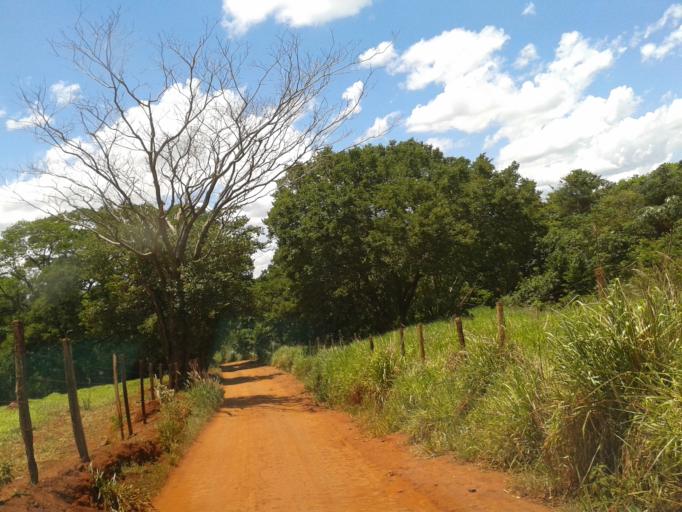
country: BR
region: Minas Gerais
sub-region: Centralina
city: Centralina
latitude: -18.6984
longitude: -49.1701
